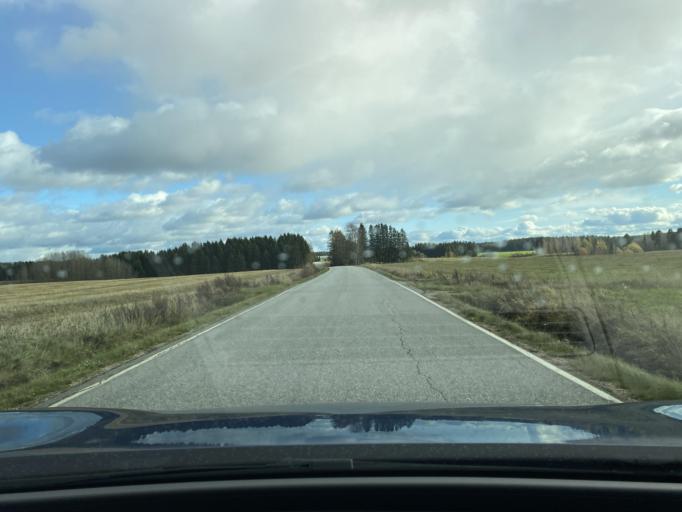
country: FI
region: Varsinais-Suomi
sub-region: Loimaa
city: Aura
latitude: 60.7035
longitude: 22.5953
